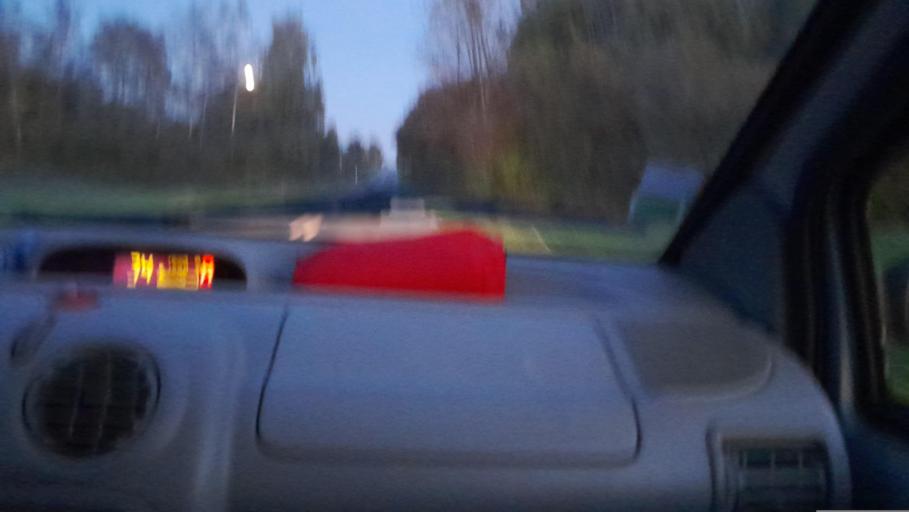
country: FR
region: Brittany
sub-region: Departement d'Ille-et-Vilaine
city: La Guerche-de-Bretagne
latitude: 47.9016
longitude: -1.1558
